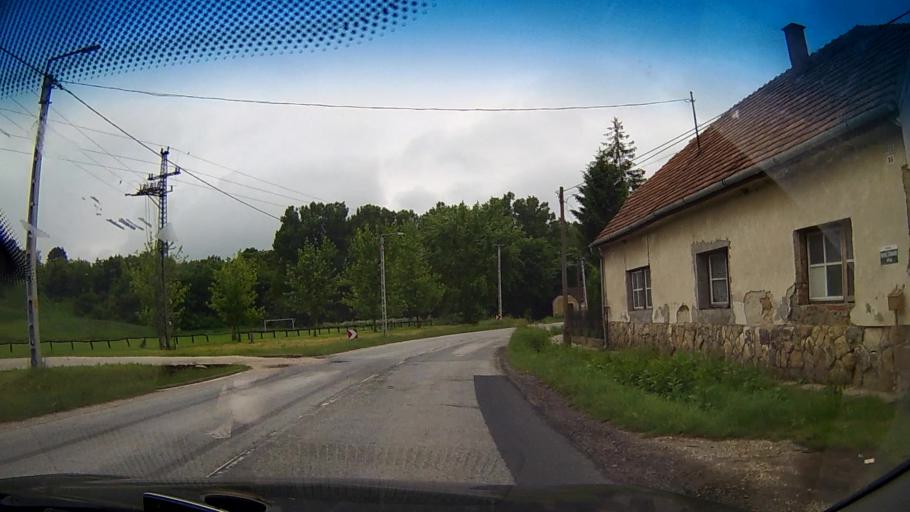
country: HU
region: Pest
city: Perbal
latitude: 47.6176
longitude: 18.7801
